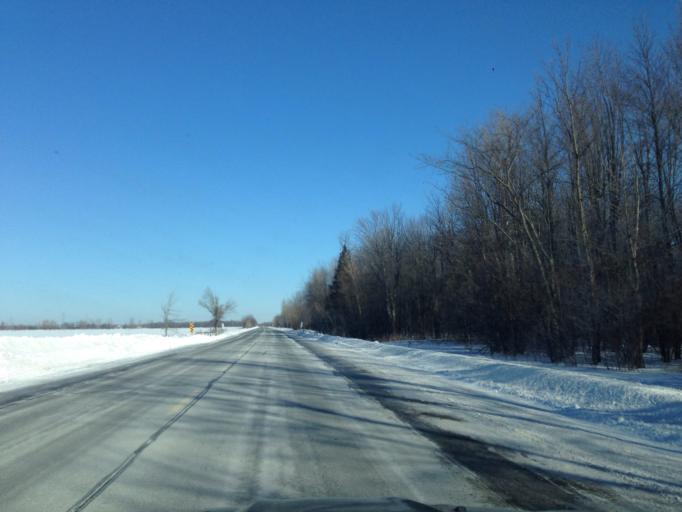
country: CA
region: Ontario
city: Clarence-Rockland
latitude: 45.3037
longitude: -75.4216
